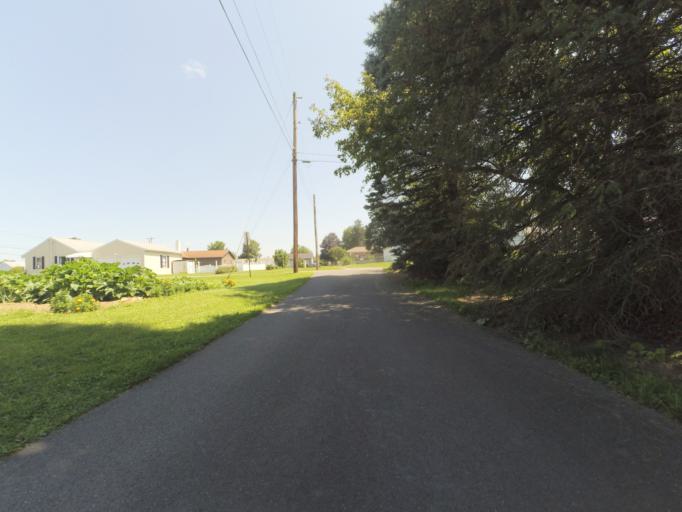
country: US
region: Pennsylvania
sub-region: Centre County
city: Pleasant Gap
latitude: 40.8641
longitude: -77.7508
